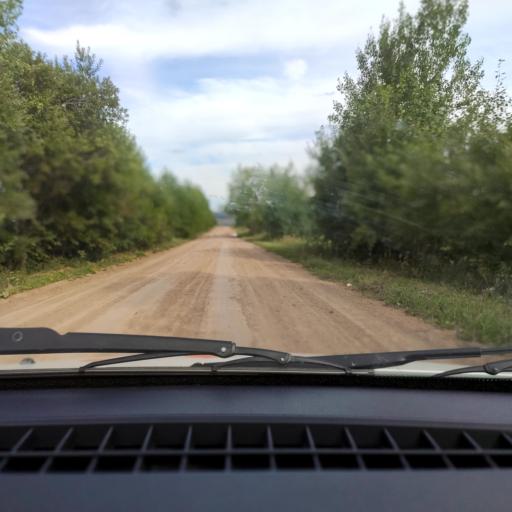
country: RU
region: Bashkortostan
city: Blagoveshchensk
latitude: 55.0990
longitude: 55.8086
